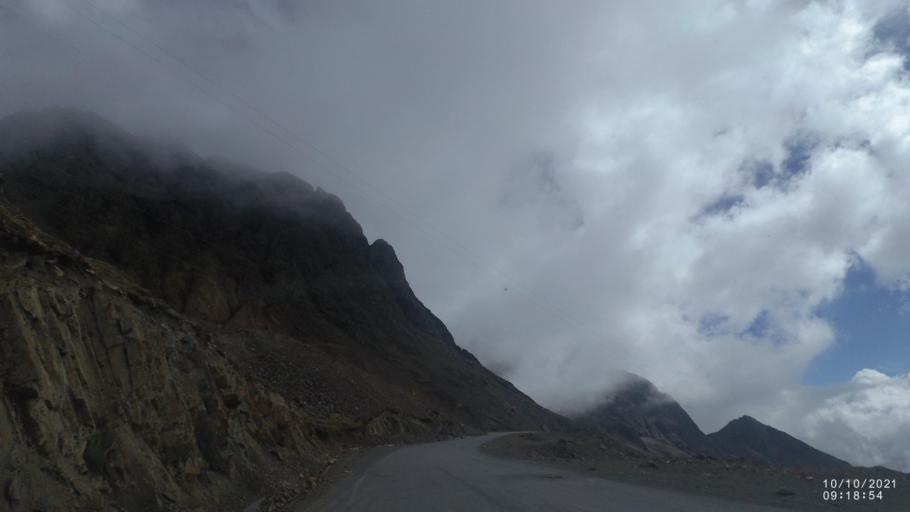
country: BO
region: La Paz
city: Quime
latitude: -17.0534
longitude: -67.2992
